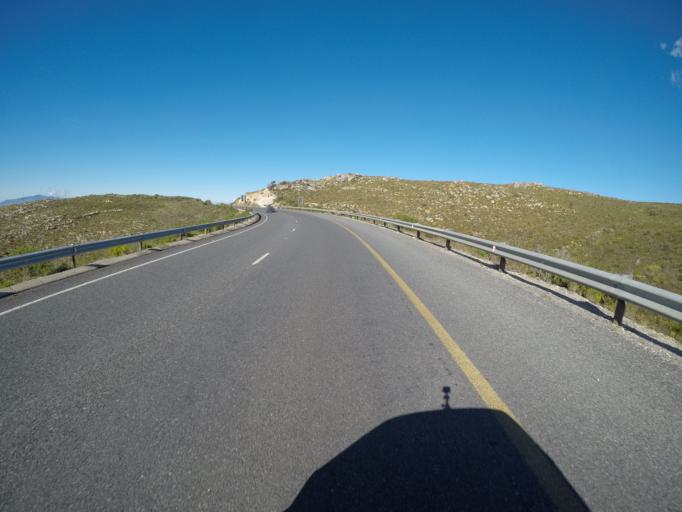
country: ZA
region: Western Cape
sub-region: Overberg District Municipality
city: Grabouw
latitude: -34.2161
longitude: 19.1699
